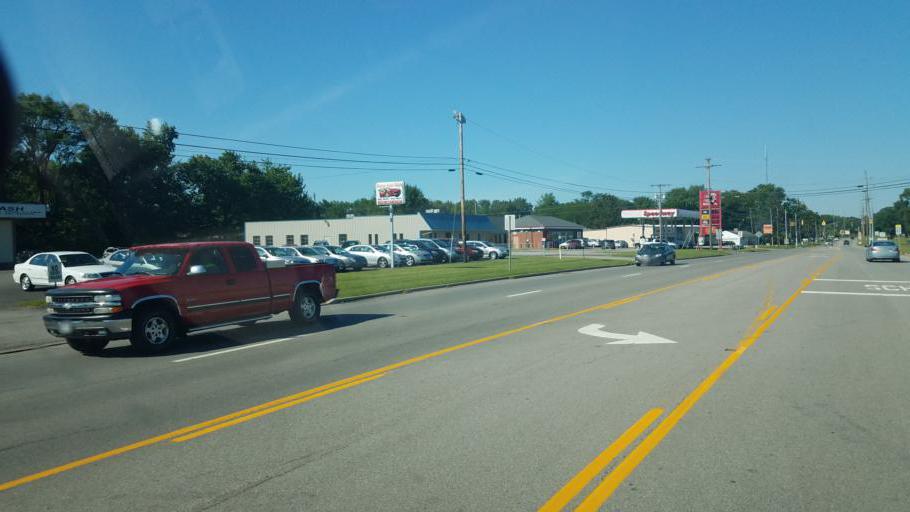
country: US
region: Ohio
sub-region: Marion County
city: Marion
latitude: 40.5936
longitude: -83.0859
